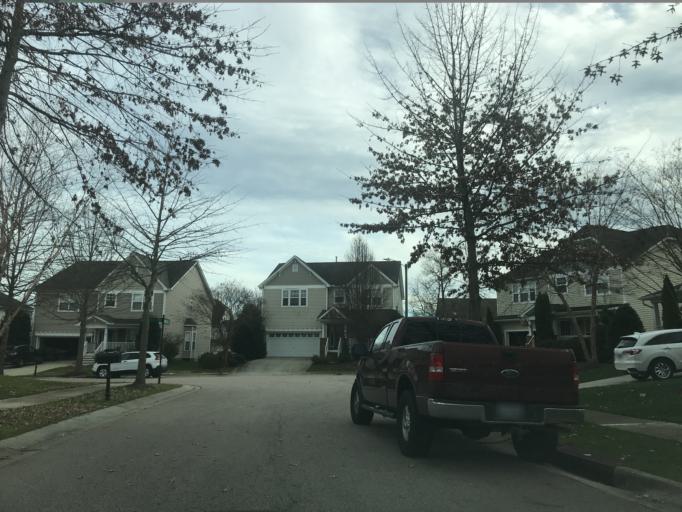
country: US
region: North Carolina
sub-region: Wake County
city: Wake Forest
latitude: 35.9245
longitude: -78.5629
